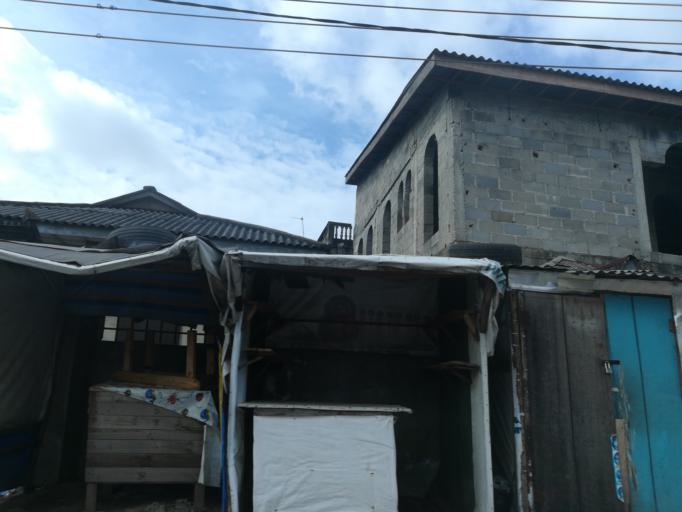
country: NG
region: Lagos
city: Somolu
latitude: 6.5439
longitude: 3.3742
